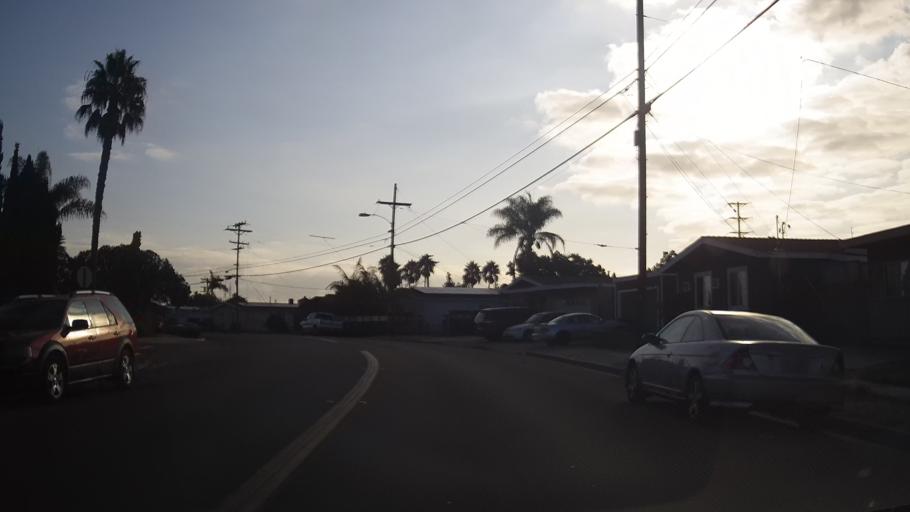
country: US
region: California
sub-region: San Diego County
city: La Jolla
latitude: 32.8355
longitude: -117.1910
